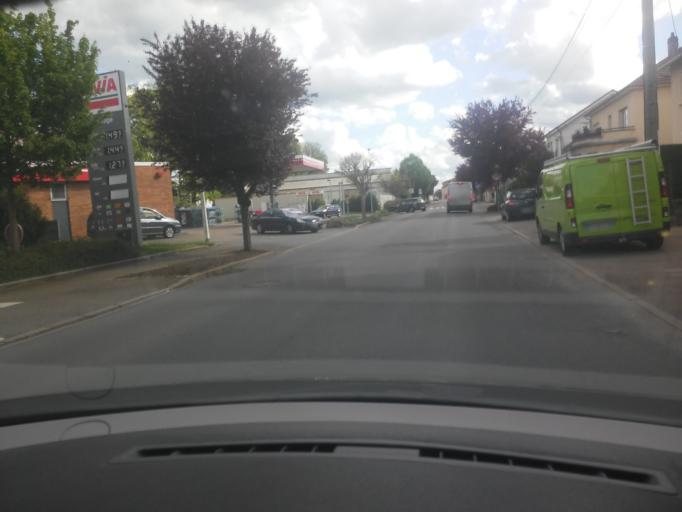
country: FR
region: Lorraine
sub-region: Departement de Meurthe-et-Moselle
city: Jarny
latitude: 49.1604
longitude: 5.8812
